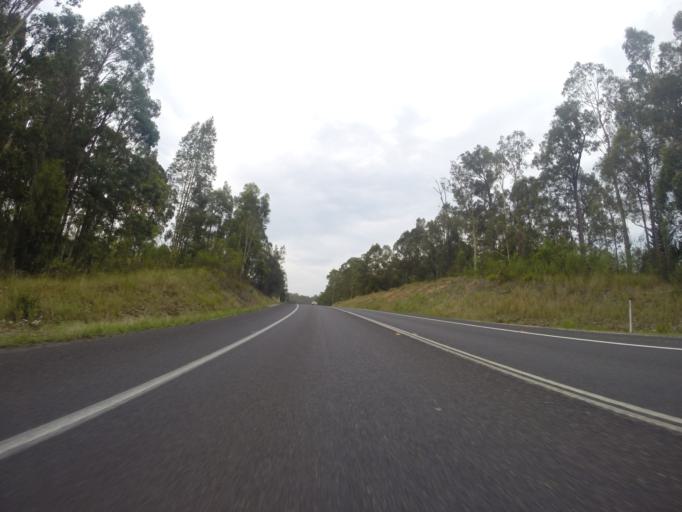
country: AU
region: New South Wales
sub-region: Eurobodalla
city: Batemans Bay
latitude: -35.6857
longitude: 150.2016
